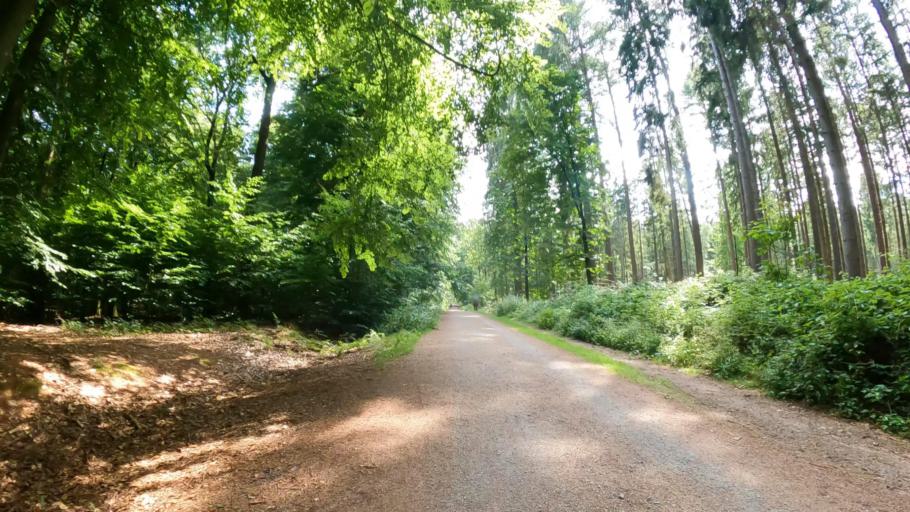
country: DE
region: Schleswig-Holstein
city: Huttblek
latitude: 53.8100
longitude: 10.0732
